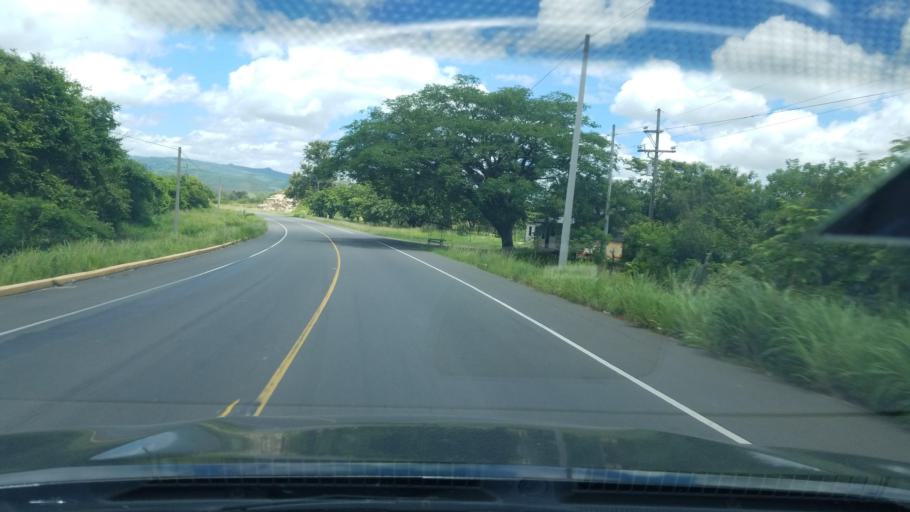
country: HN
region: Francisco Morazan
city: Cofradia
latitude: 14.2944
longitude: -87.2419
